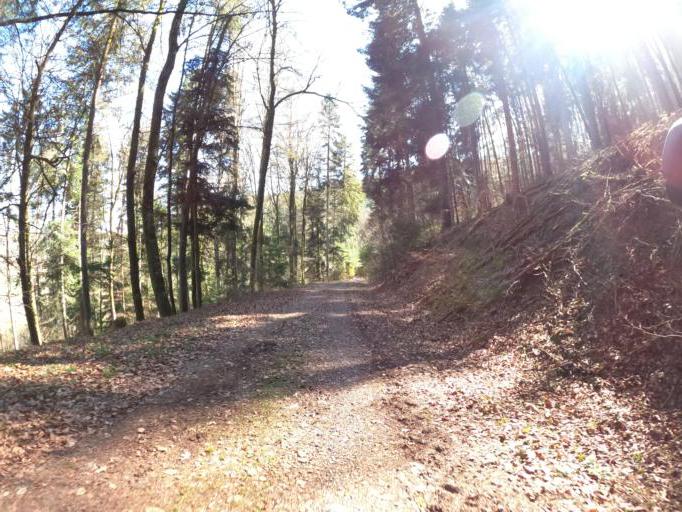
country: DE
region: Baden-Wuerttemberg
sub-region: Tuebingen Region
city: Haigerloch
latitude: 48.3908
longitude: 8.7800
